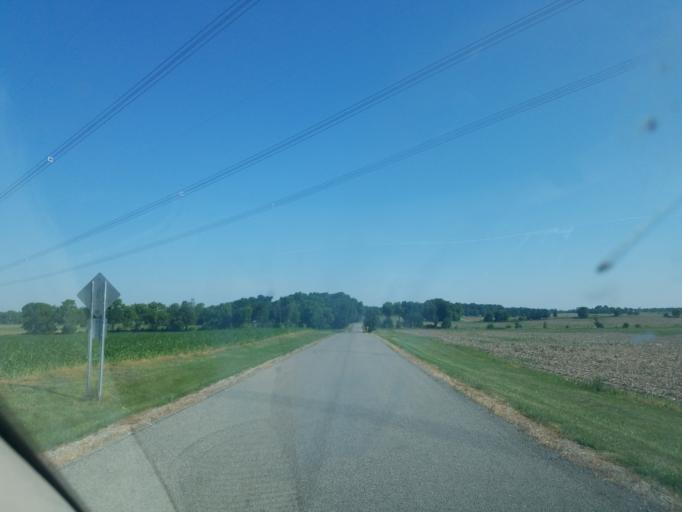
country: US
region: Ohio
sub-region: Logan County
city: Northwood
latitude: 40.4302
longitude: -83.6710
